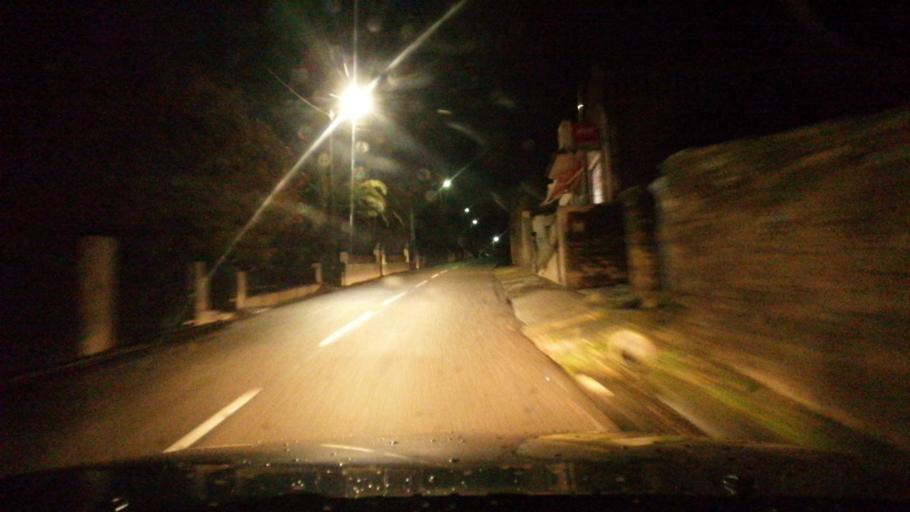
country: PT
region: Viseu
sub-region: Sao Joao da Pesqueira
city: Sao Joao da Pesqueira
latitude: 41.0813
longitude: -7.4331
